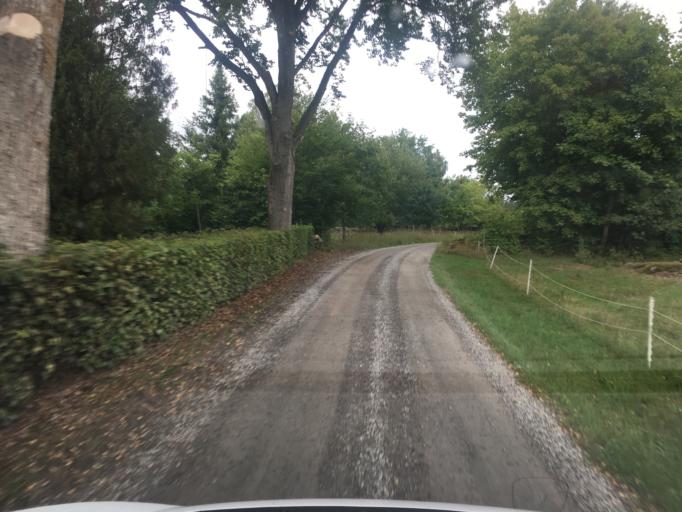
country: SE
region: Kronoberg
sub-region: Ljungby Kommun
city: Lagan
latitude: 56.9558
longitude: 14.0411
